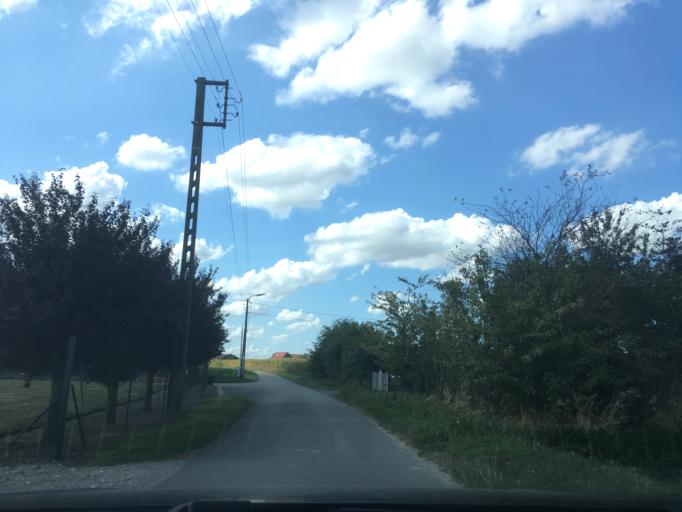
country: BE
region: Flanders
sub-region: Provincie West-Vlaanderen
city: Staden
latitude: 50.9749
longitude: 3.0459
